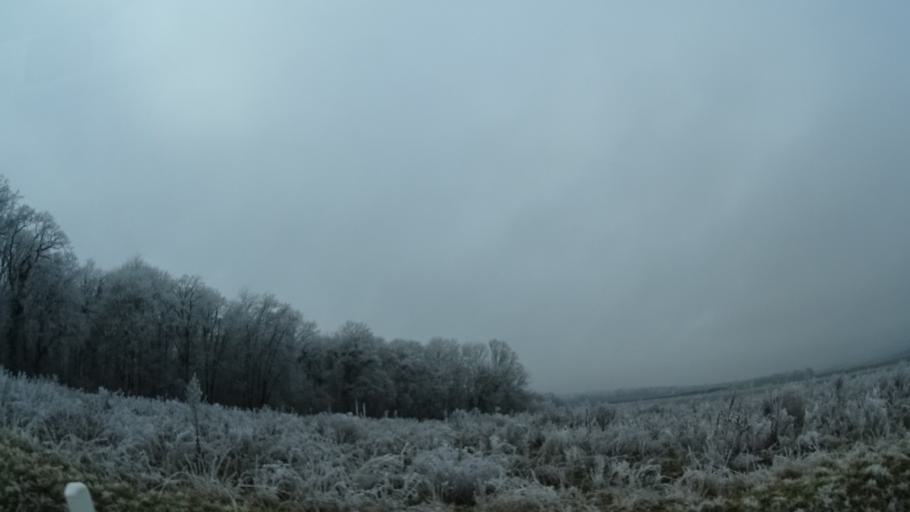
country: DE
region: Bavaria
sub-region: Regierungsbezirk Unterfranken
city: Butthard
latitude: 49.5873
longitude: 9.8710
